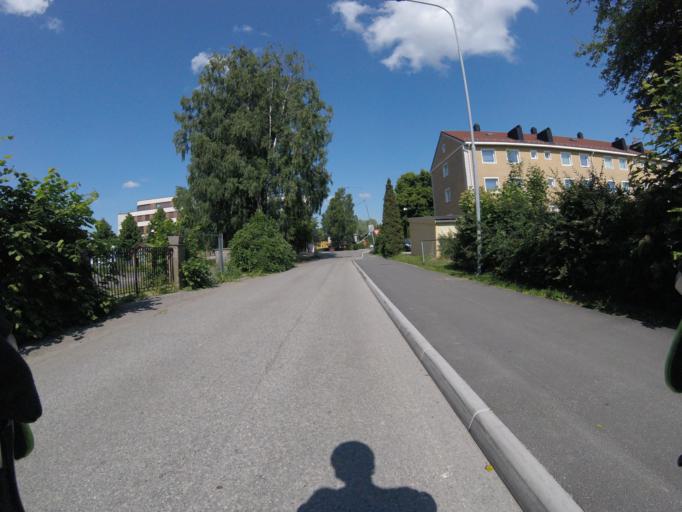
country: NO
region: Akershus
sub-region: Skedsmo
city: Lillestrom
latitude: 59.9581
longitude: 11.0540
